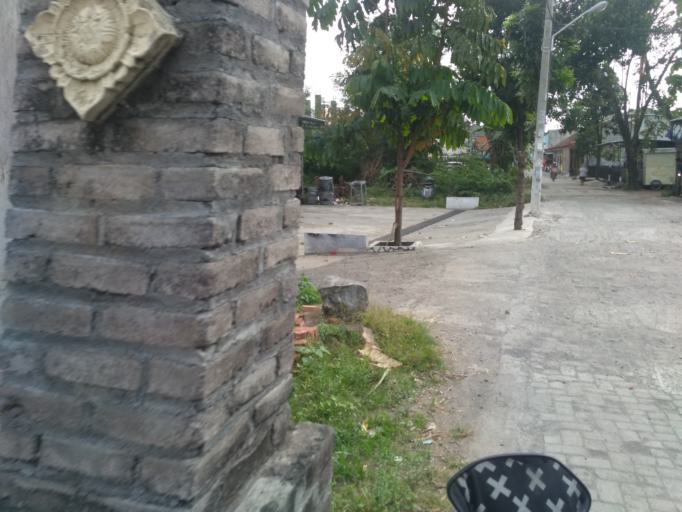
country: ID
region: Daerah Istimewa Yogyakarta
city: Depok
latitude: -7.7744
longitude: 110.4059
